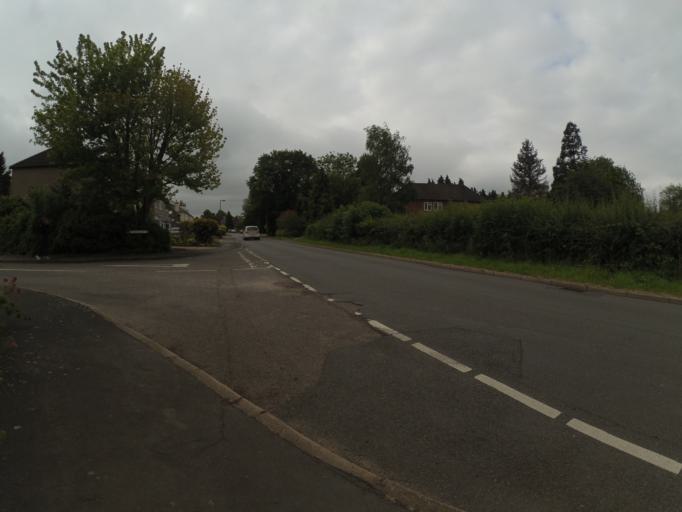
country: GB
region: England
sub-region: Warwickshire
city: Dunchurch
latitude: 52.3415
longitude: -1.2913
